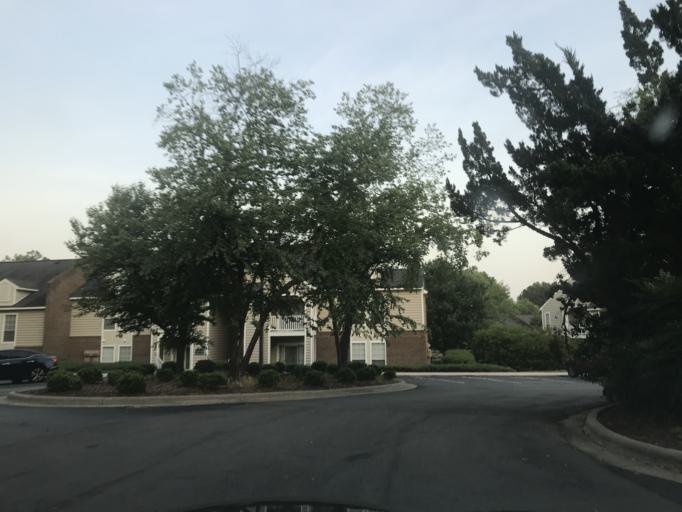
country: US
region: North Carolina
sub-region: Wake County
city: West Raleigh
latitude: 35.8804
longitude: -78.5963
